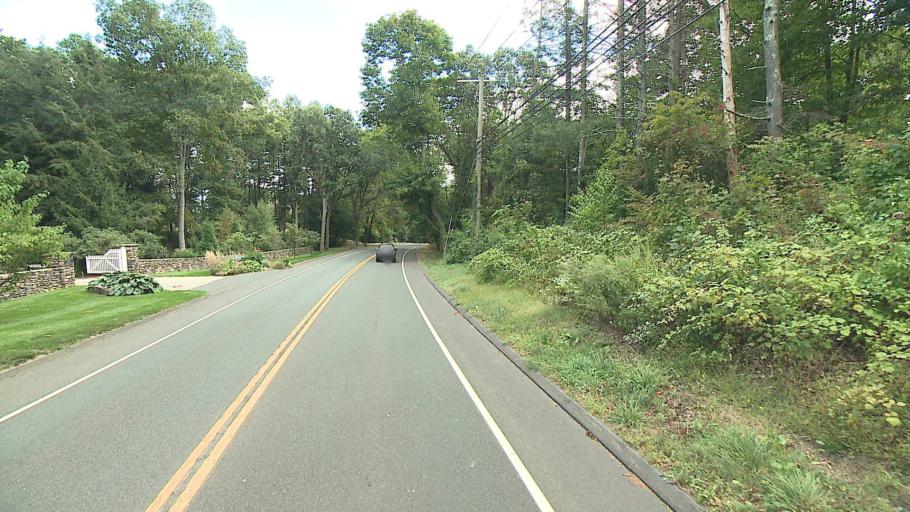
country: US
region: Connecticut
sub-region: Fairfield County
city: Westport
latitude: 41.1738
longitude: -73.3895
